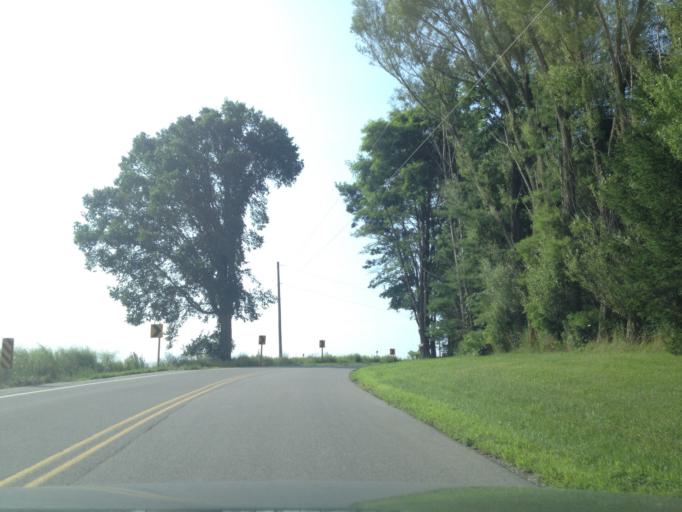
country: CA
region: Ontario
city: Aylmer
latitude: 42.7583
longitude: -80.8457
